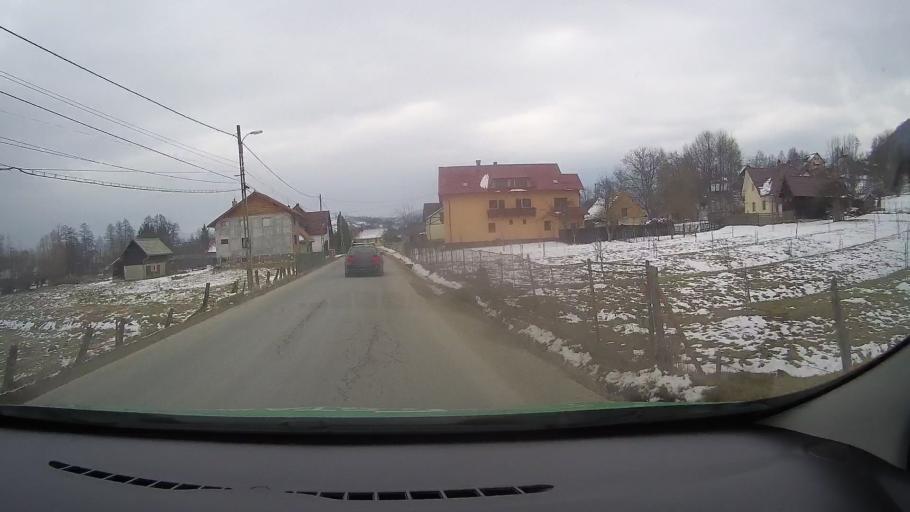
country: RO
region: Brasov
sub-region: Comuna Bran
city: Bran
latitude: 45.5292
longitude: 25.3572
